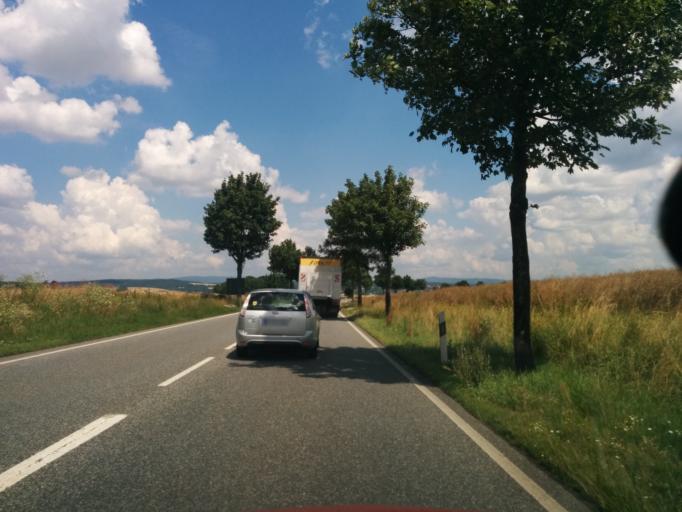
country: DE
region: Lower Saxony
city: Wollbrandshausen
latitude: 51.5904
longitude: 10.1767
